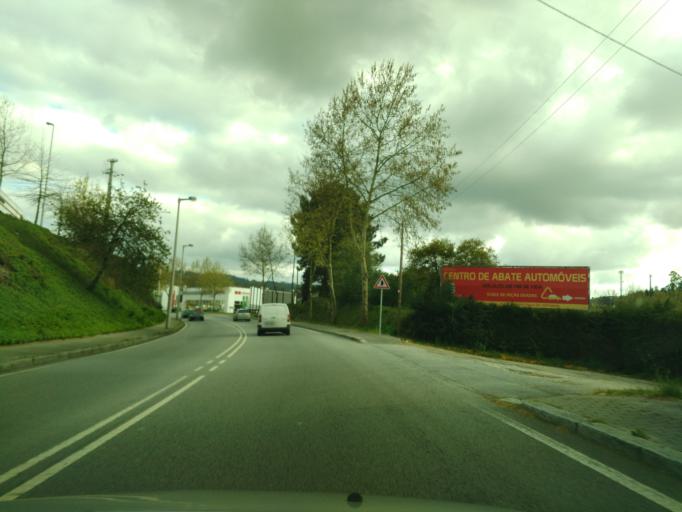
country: PT
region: Braga
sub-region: Guimaraes
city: Urgeses
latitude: 41.4255
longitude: -8.3047
